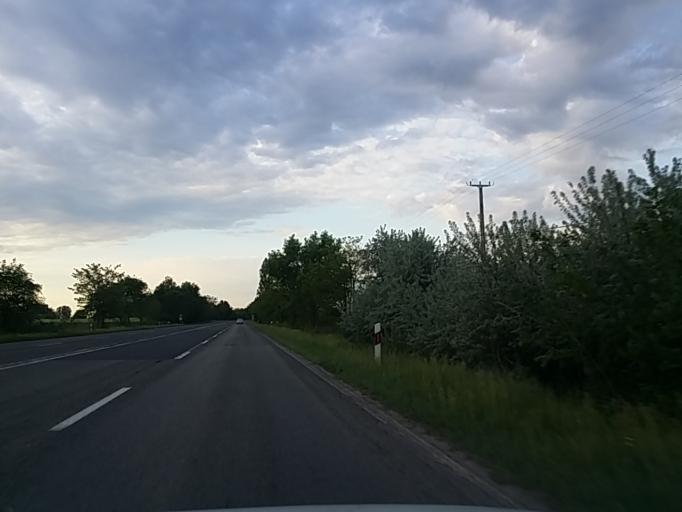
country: HU
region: Bacs-Kiskun
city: Kecskemet
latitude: 46.9585
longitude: 19.6454
